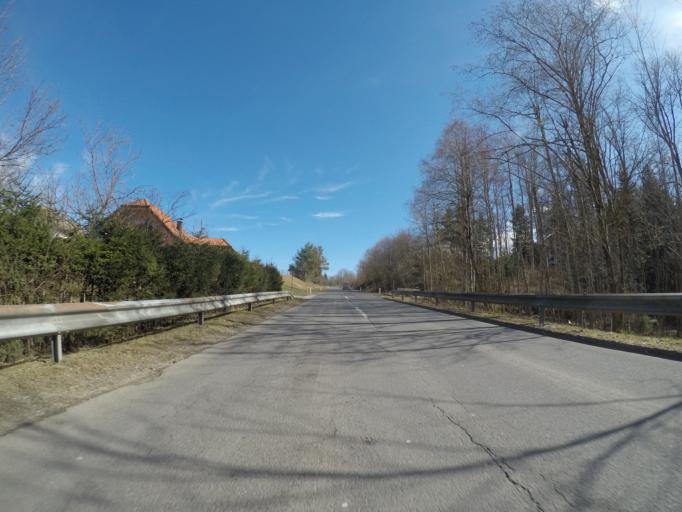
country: SI
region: Lovrenc na Pohorju
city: Lovrenc na Pohorju
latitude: 46.5414
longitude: 15.4256
